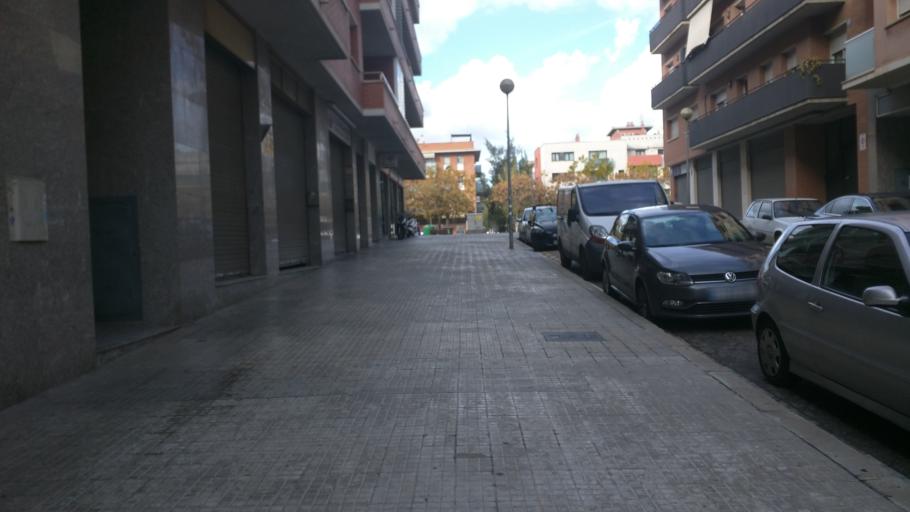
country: ES
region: Catalonia
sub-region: Provincia de Barcelona
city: Molins de Rei
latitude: 41.4155
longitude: 2.0137
